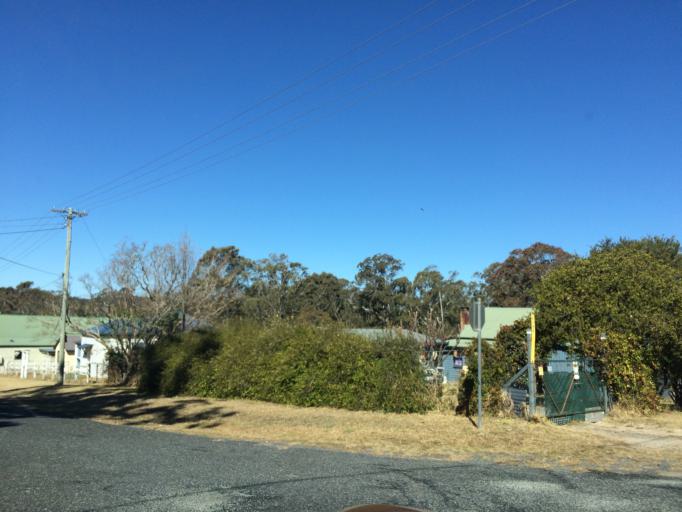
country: AU
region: Queensland
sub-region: Southern Downs
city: Stanthorpe
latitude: -28.6467
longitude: 152.0849
